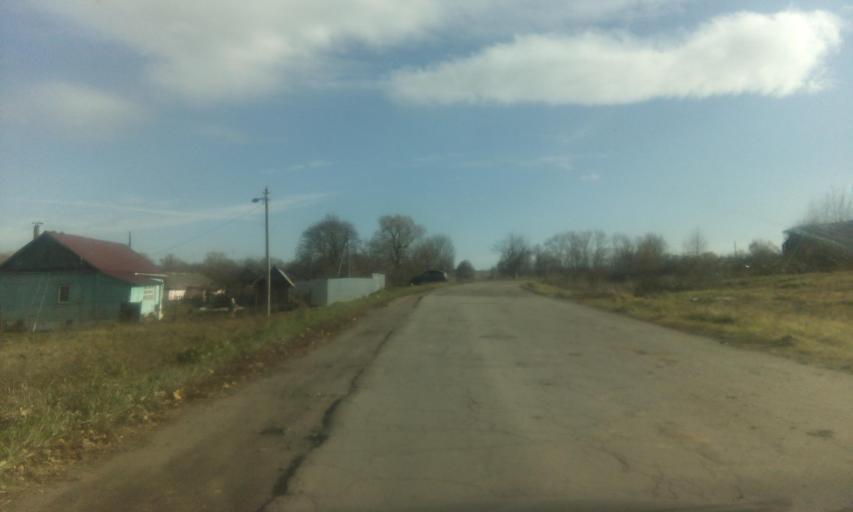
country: RU
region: Tula
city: Dubovka
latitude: 53.9461
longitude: 38.0341
